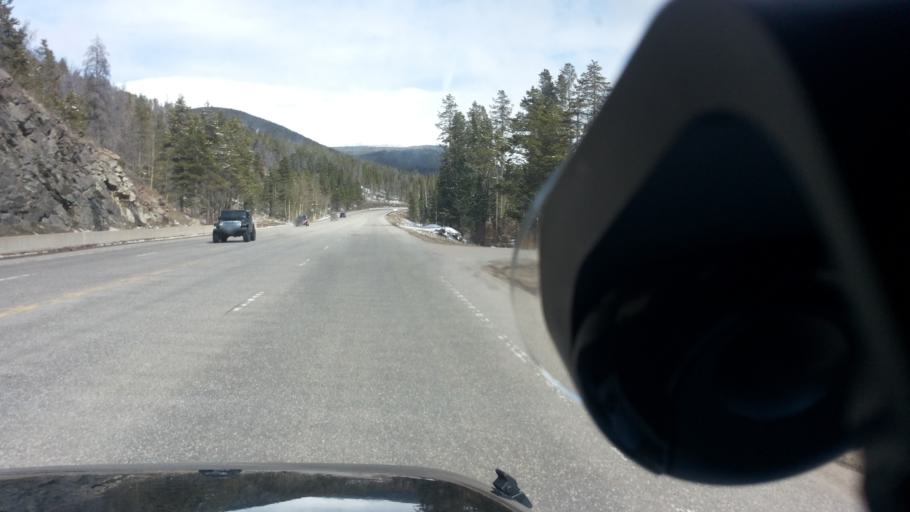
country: US
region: Colorado
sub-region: Grand County
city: Fraser
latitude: 39.8989
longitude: -105.7744
